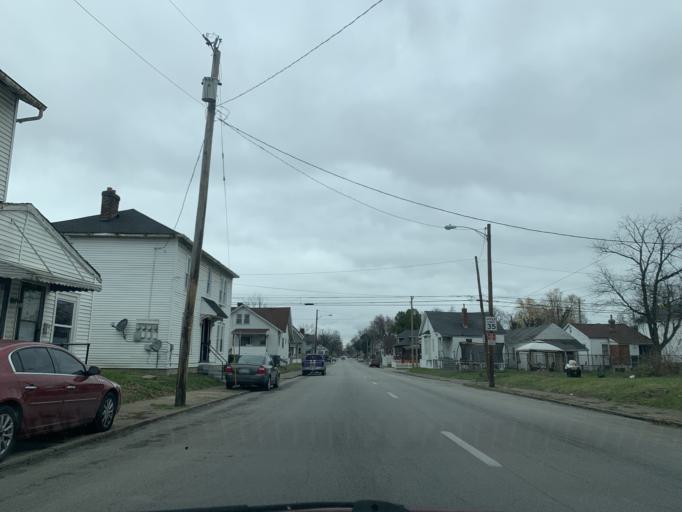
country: US
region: Kentucky
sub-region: Jefferson County
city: Louisville
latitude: 38.2374
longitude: -85.7886
